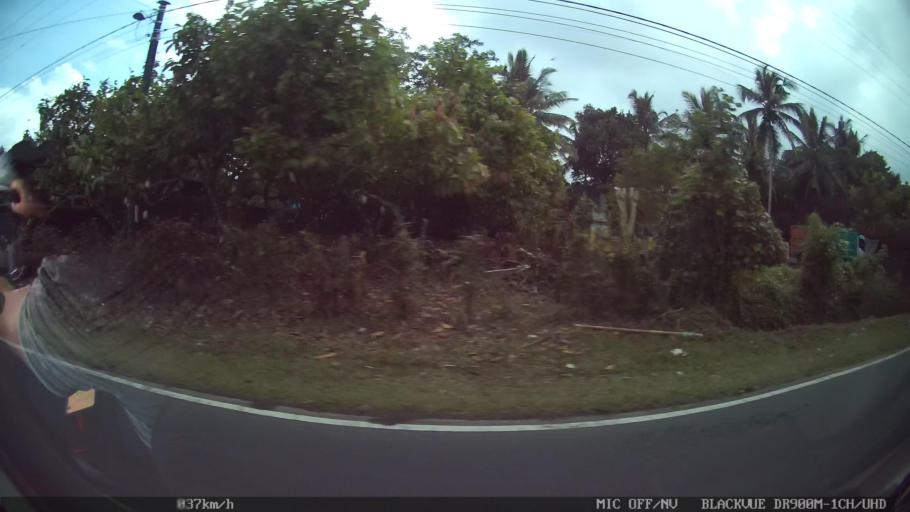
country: ID
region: Bali
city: Pohgending Kawan
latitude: -8.4523
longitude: 115.1388
